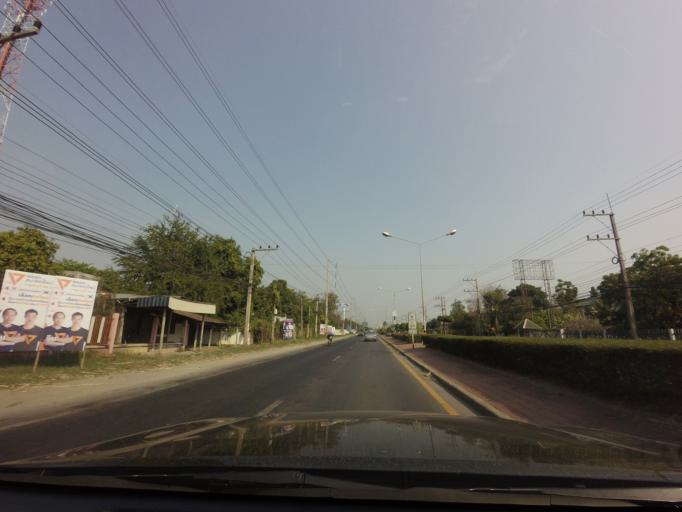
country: TH
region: Kanchanaburi
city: Tha Maka
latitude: 13.9017
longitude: 99.7870
